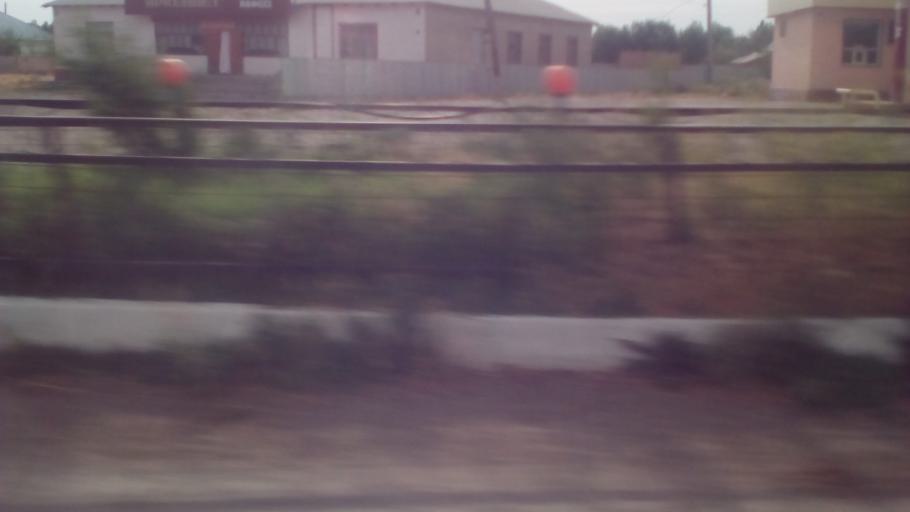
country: KZ
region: Ongtustik Qazaqstan
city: Shayan
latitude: 43.0459
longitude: 69.3896
